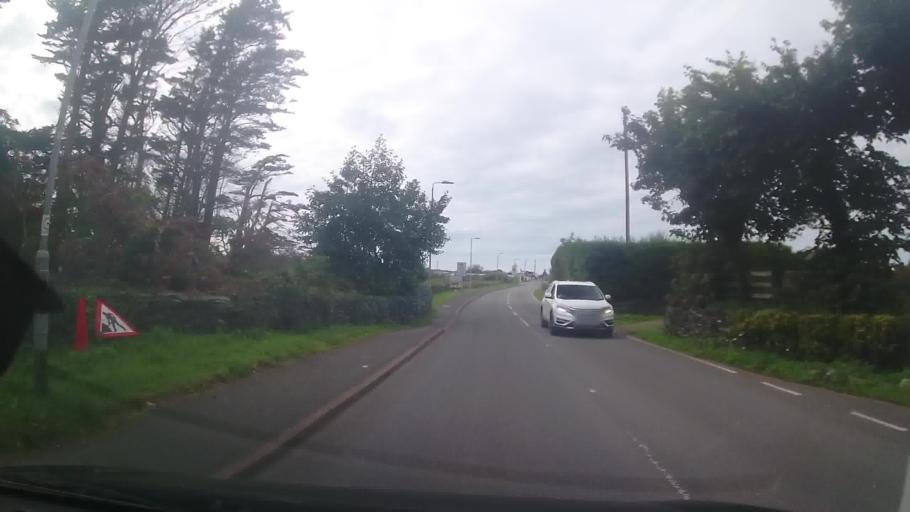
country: GB
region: Wales
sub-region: Gwynedd
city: Barmouth
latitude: 52.6946
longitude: -4.0469
